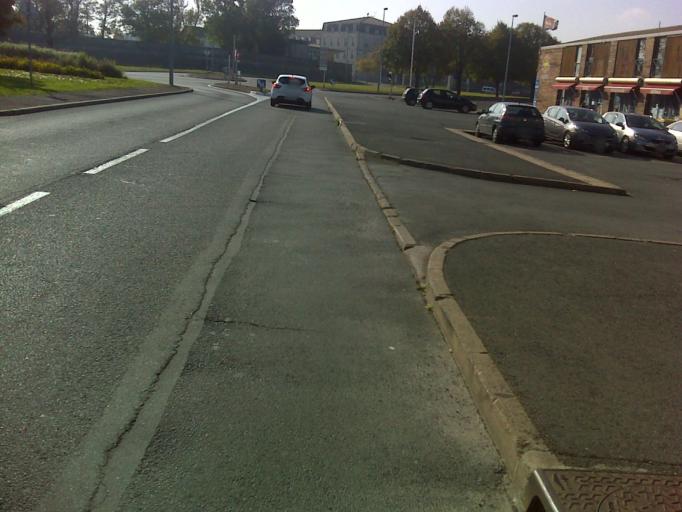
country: FR
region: Poitou-Charentes
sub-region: Departement de la Charente-Maritime
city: Rochefort
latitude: 45.9454
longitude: -0.9579
